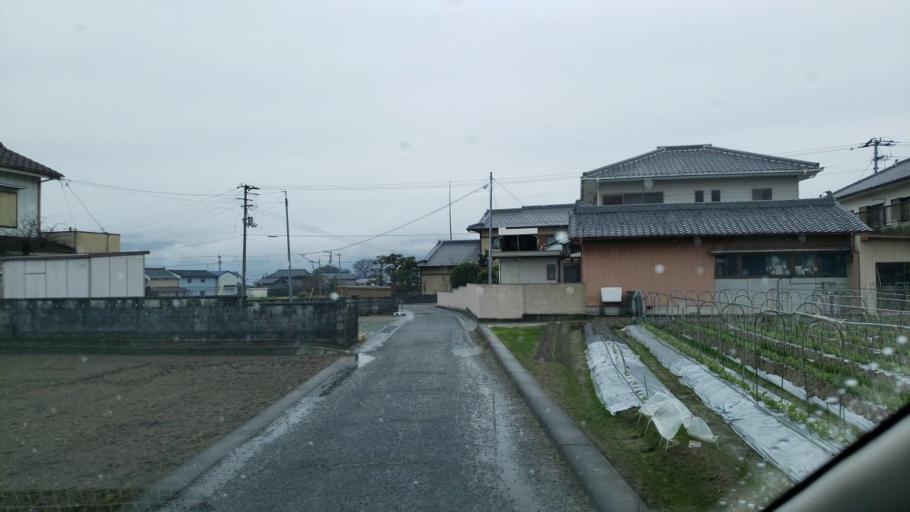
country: JP
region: Tokushima
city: Kamojimacho-jogejima
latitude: 34.0824
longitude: 134.2569
